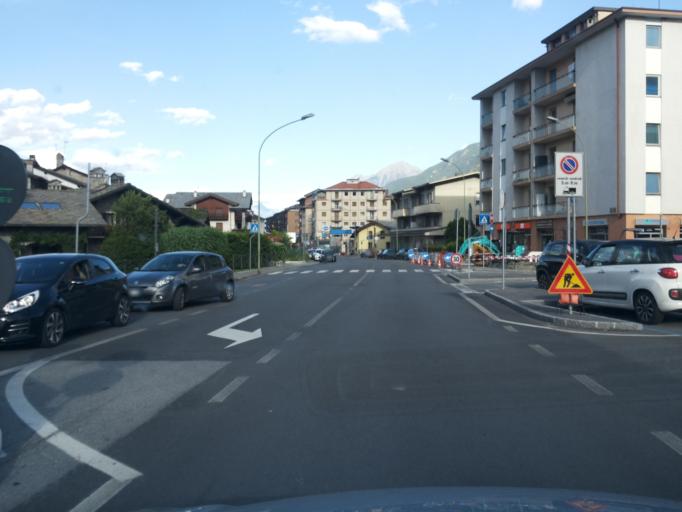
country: IT
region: Aosta Valley
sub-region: Valle d'Aosta
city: Aosta
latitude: 45.7394
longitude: 7.3296
